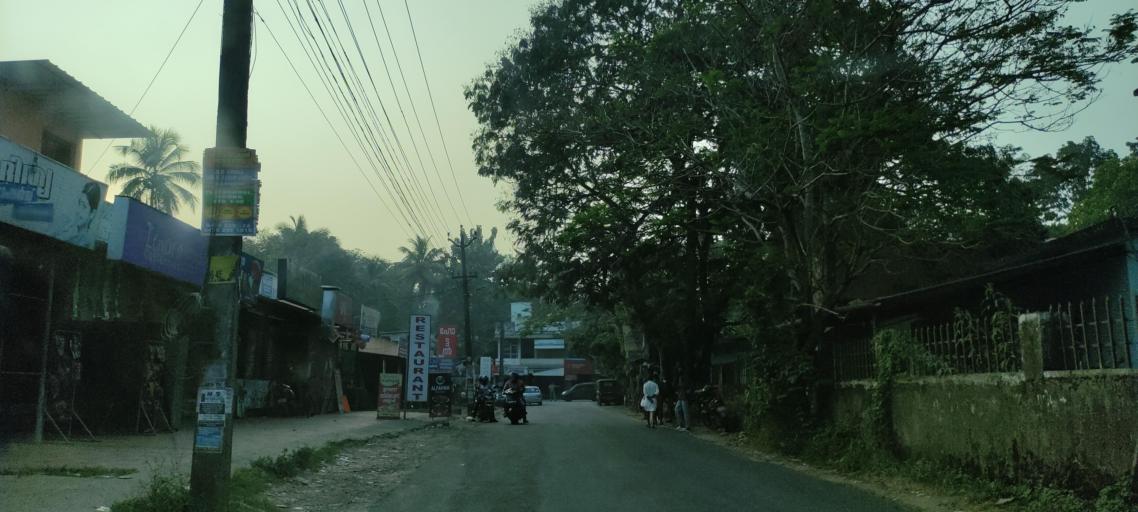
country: IN
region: Kerala
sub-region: Kottayam
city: Vaikam
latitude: 9.6868
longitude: 76.4207
